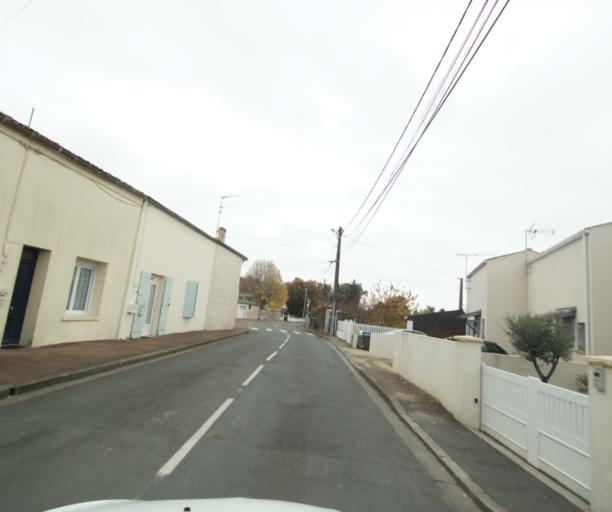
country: FR
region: Poitou-Charentes
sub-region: Departement de la Charente-Maritime
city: Saintes
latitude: 45.7355
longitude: -0.6231
